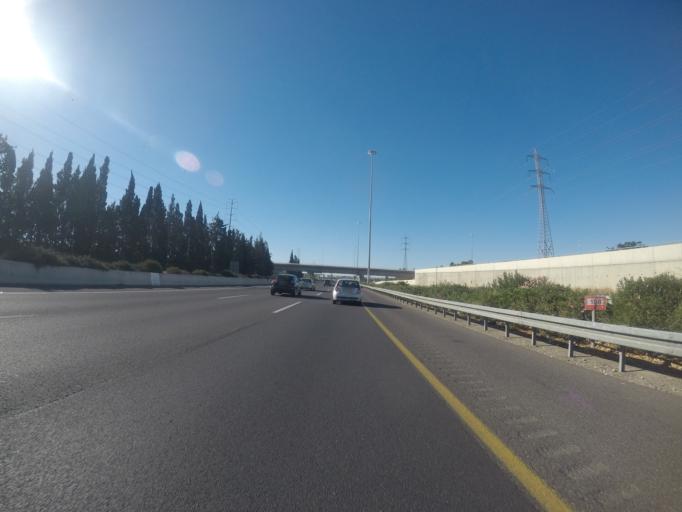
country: IL
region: Central District
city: Bet Dagan
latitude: 32.0011
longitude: 34.8061
